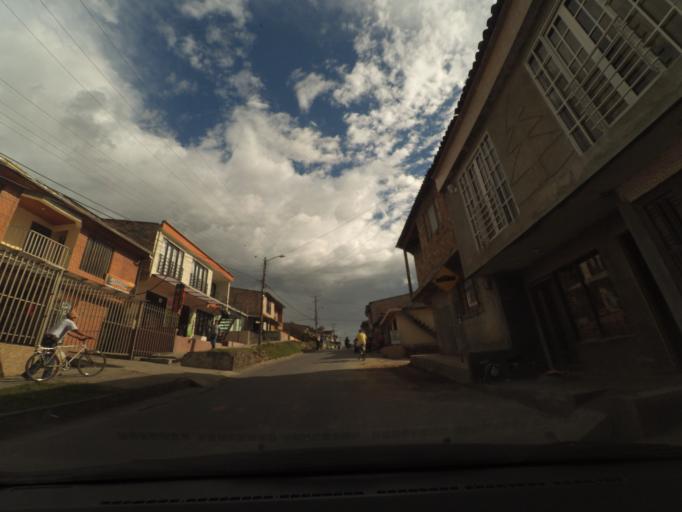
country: CO
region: Cauca
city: Popayan
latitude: 2.4449
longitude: -76.6250
